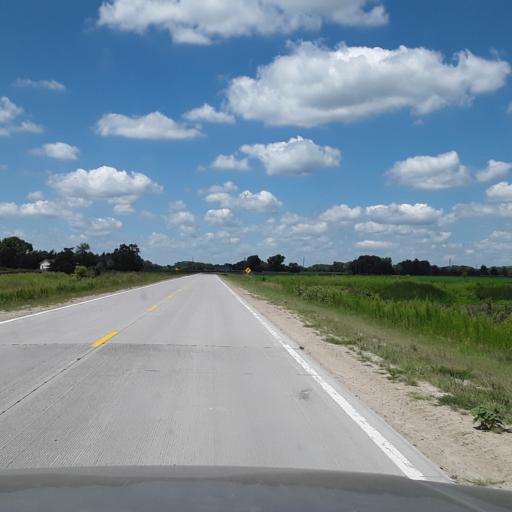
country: US
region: Nebraska
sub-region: Nance County
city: Genoa
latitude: 41.4255
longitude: -97.7302
